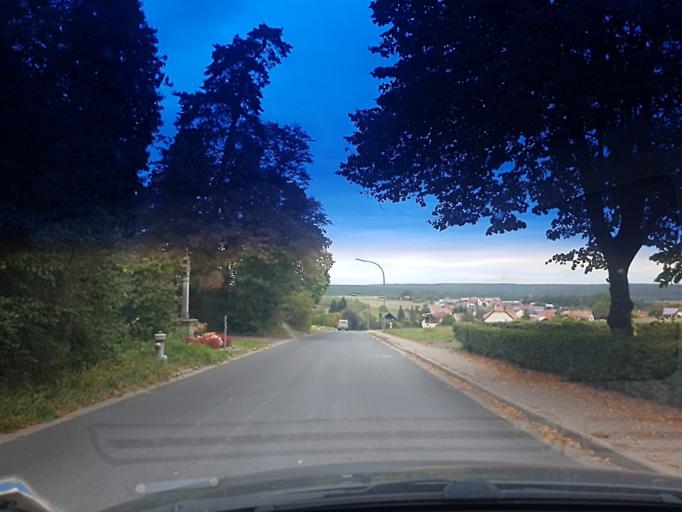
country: DE
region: Bavaria
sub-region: Regierungsbezirk Unterfranken
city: Geiselwind
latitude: 49.8263
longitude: 10.4849
